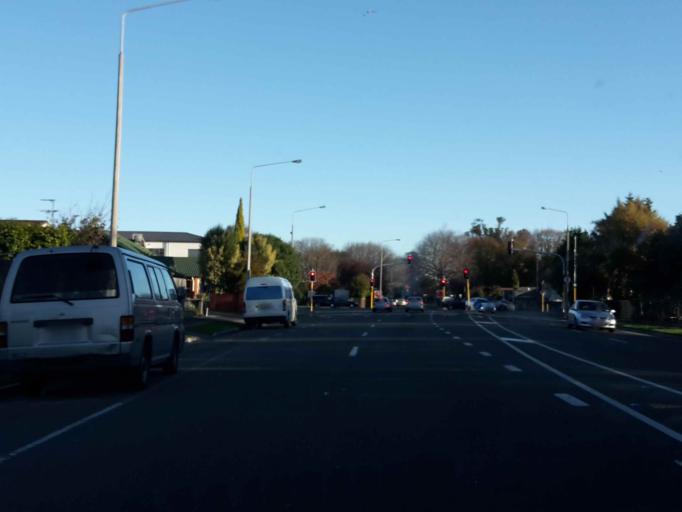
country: NZ
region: Canterbury
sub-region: Christchurch City
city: Christchurch
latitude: -43.5298
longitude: 172.5688
